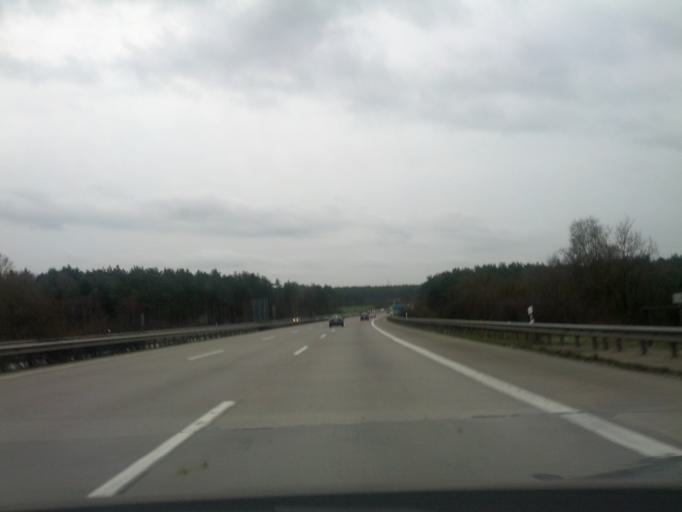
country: DE
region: Lower Saxony
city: Egestorf
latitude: 53.1855
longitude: 10.0832
